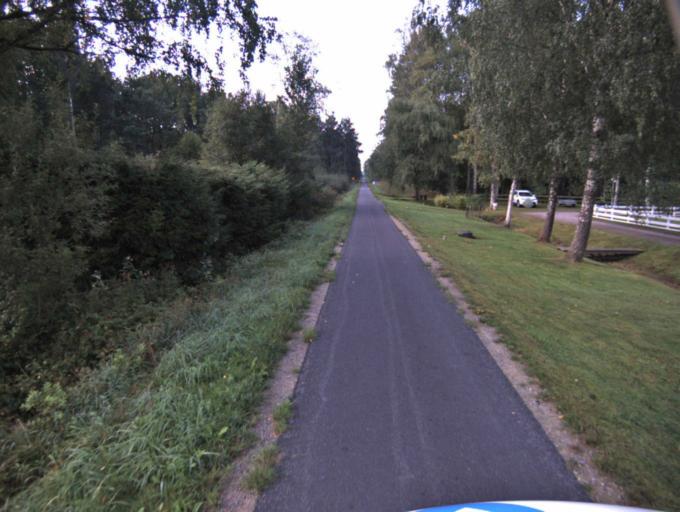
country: SE
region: Vaestra Goetaland
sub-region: Ulricehamns Kommun
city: Ulricehamn
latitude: 57.7196
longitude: 13.3996
